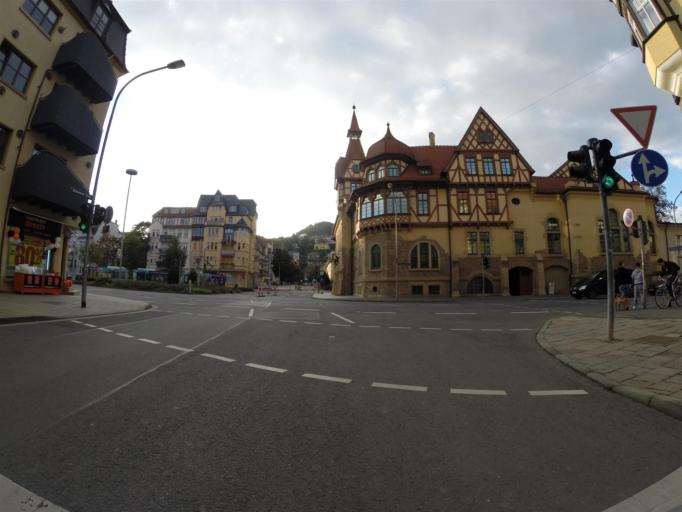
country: DE
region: Thuringia
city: Jena
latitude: 50.9360
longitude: 11.5898
